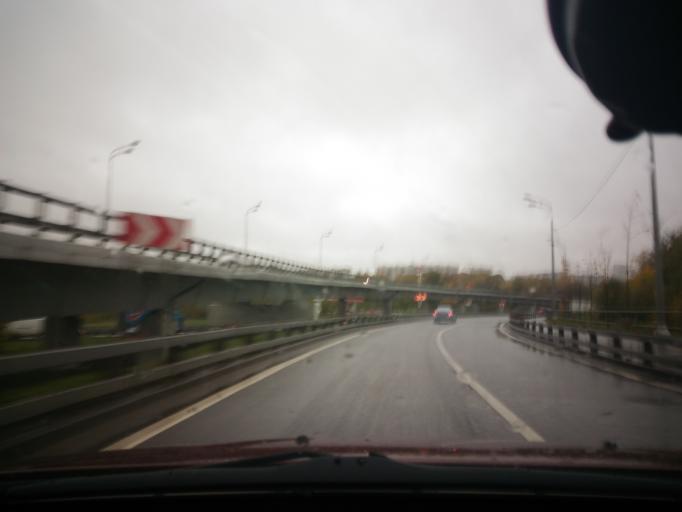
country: RU
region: Moskovskaya
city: Pavshino
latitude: 55.8289
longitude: 37.3745
